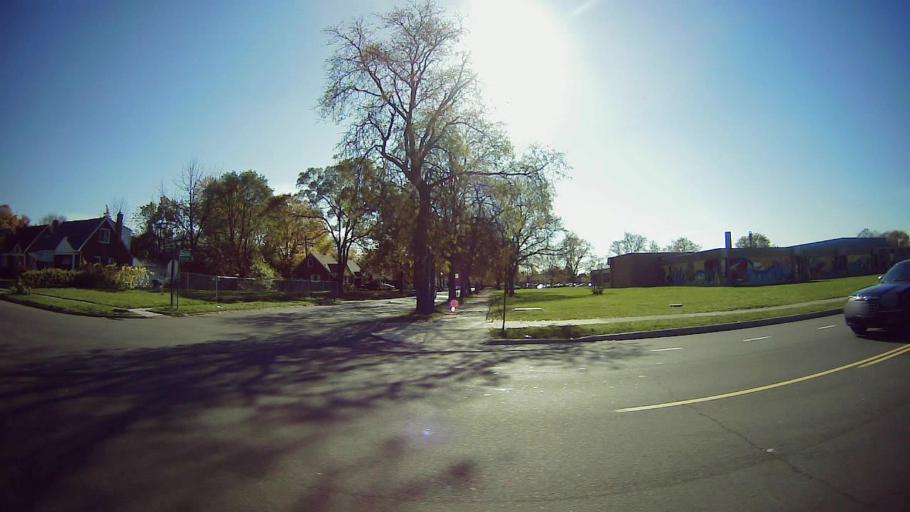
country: US
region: Michigan
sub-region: Wayne County
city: Dearborn
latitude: 42.3653
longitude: -83.2041
